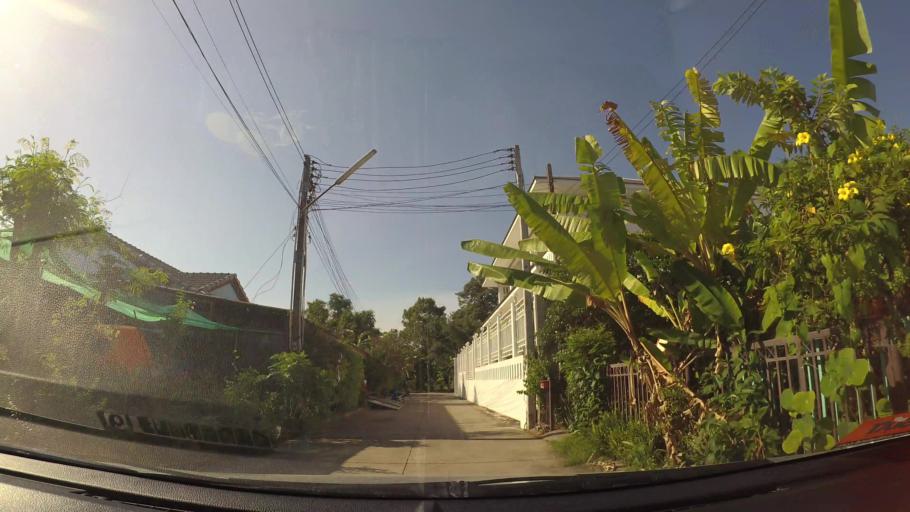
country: TH
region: Chon Buri
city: Si Racha
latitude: 13.1542
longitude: 100.9362
